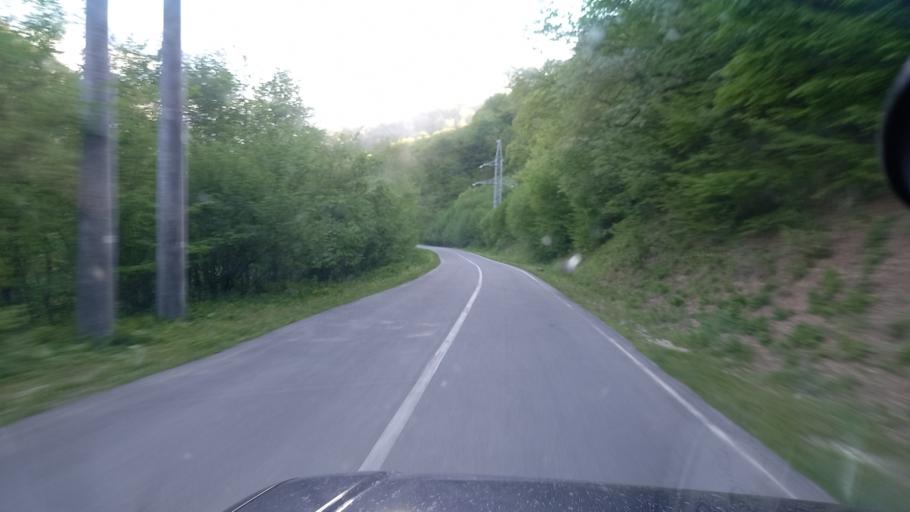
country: RU
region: North Ossetia
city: Tarskoye
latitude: 42.9015
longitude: 44.9494
